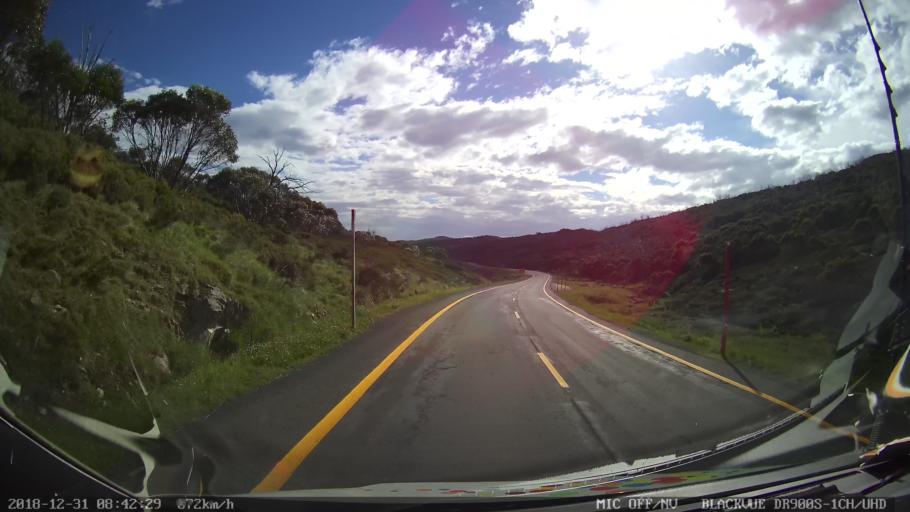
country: AU
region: New South Wales
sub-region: Snowy River
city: Jindabyne
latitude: -36.3932
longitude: 148.4330
